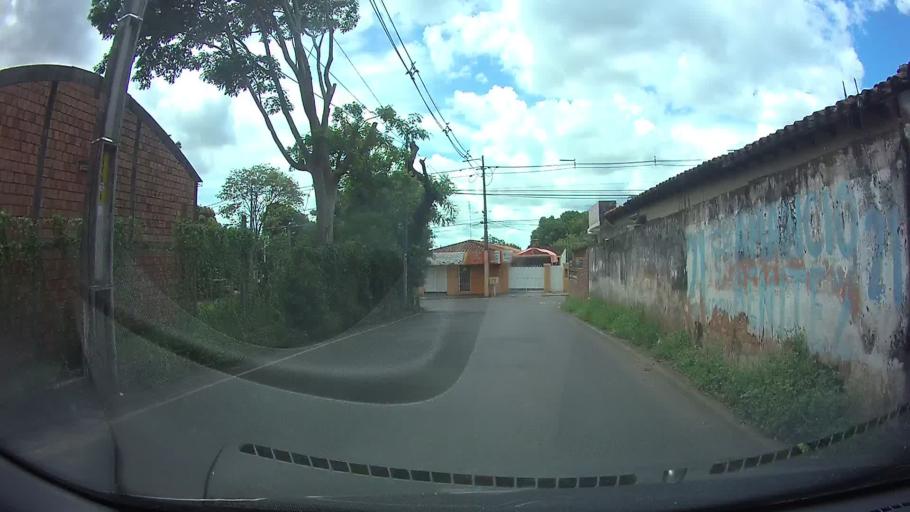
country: PY
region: Central
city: Fernando de la Mora
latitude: -25.3230
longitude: -57.5482
